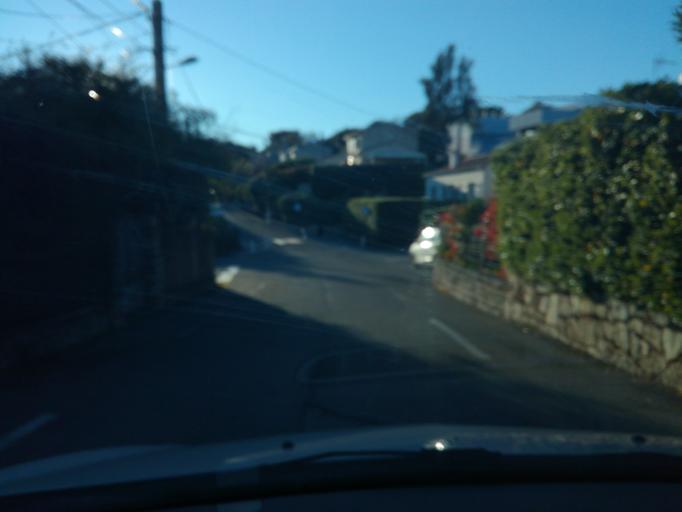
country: FR
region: Provence-Alpes-Cote d'Azur
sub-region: Departement des Alpes-Maritimes
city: Grasse
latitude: 43.6402
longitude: 6.9165
